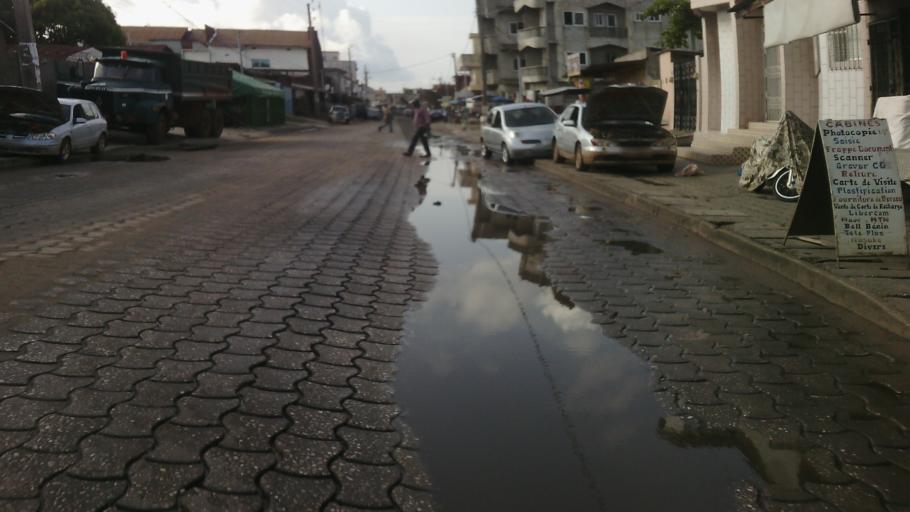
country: BJ
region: Atlantique
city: Abomey-Calavi
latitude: 6.3899
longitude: 2.3642
